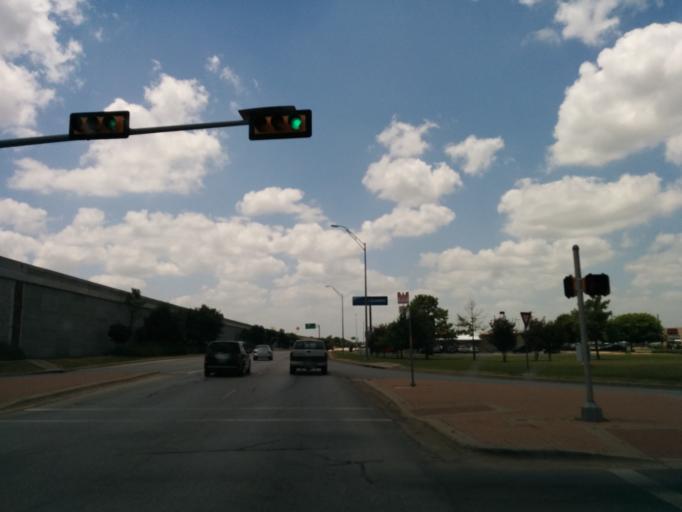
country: US
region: Texas
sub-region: Bastrop County
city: Bastrop
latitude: 30.1055
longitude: -97.3289
